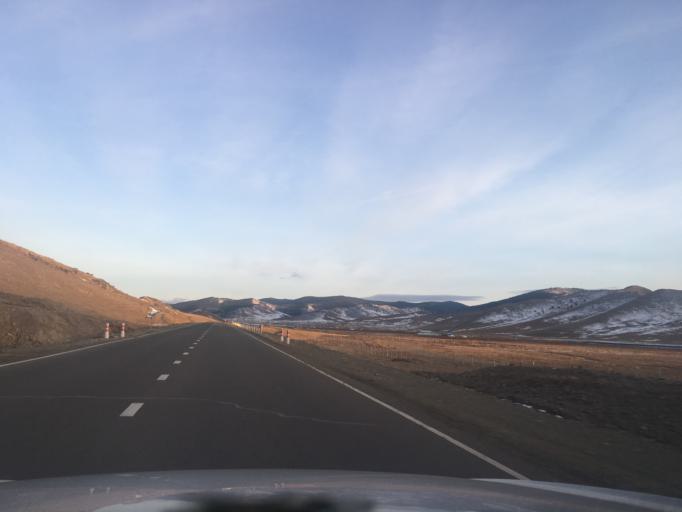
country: MN
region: Central Aimak
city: Mandal
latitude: 48.1125
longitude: 106.7062
